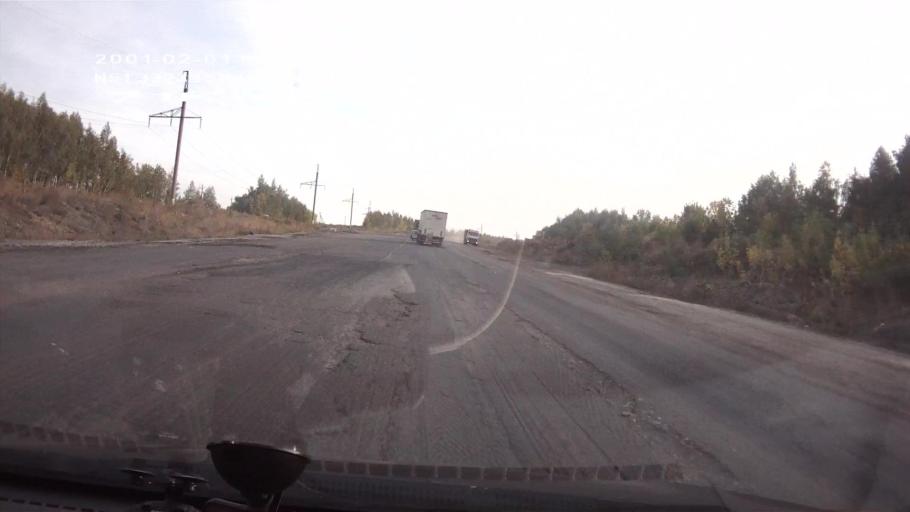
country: RU
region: Saratov
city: Krasnyy Oktyabr'
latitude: 51.3315
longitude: 45.7132
